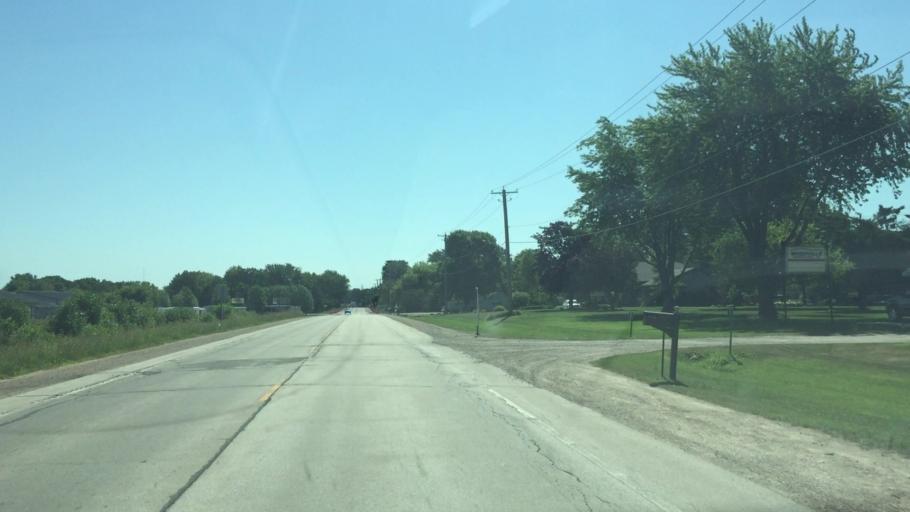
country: US
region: Wisconsin
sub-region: Calumet County
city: Hilbert
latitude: 44.1401
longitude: -88.1738
